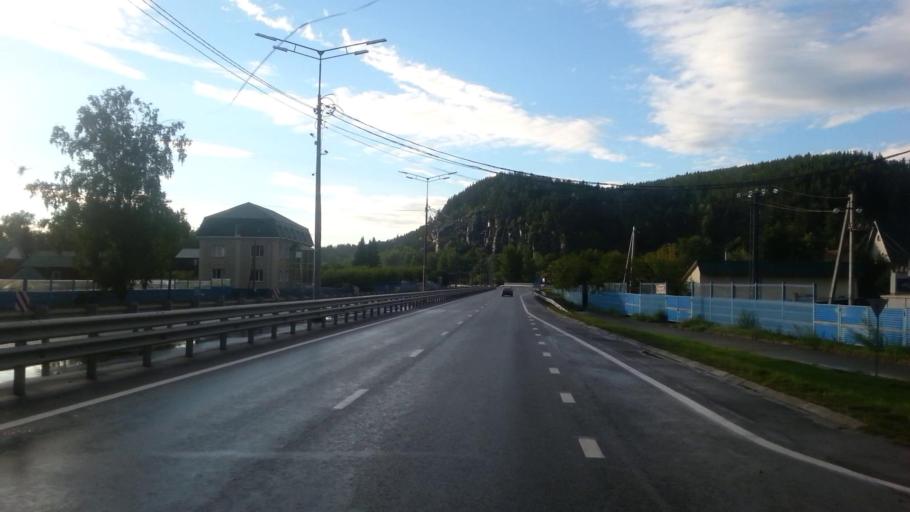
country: RU
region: Altay
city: Souzga
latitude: 51.9156
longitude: 85.8616
